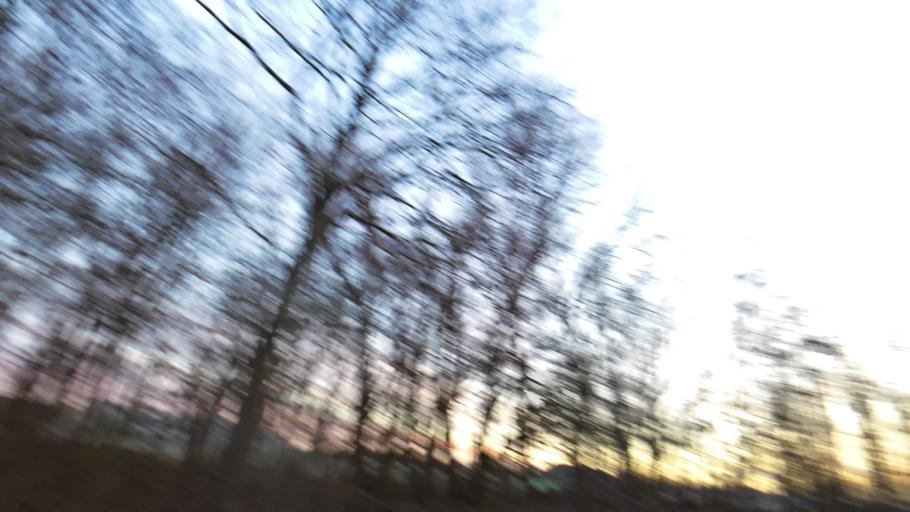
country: NL
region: South Holland
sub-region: Gemeente Noordwijkerhout
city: Noordwijkerhout
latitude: 52.2745
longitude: 4.4907
